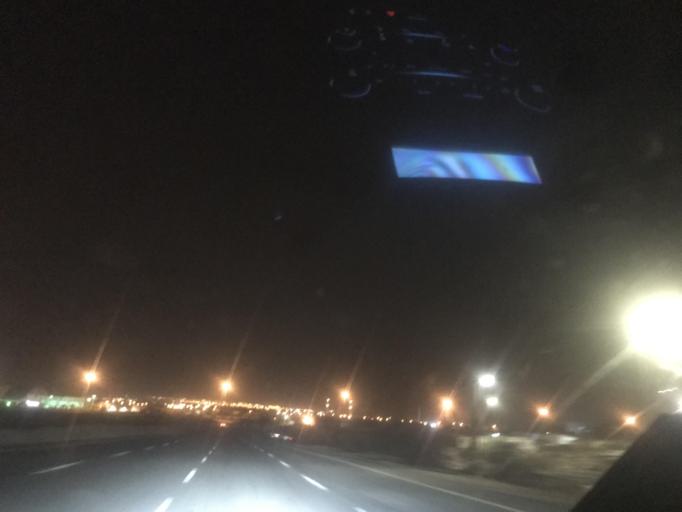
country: SA
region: Ar Riyad
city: Riyadh
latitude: 24.7613
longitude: 46.5851
